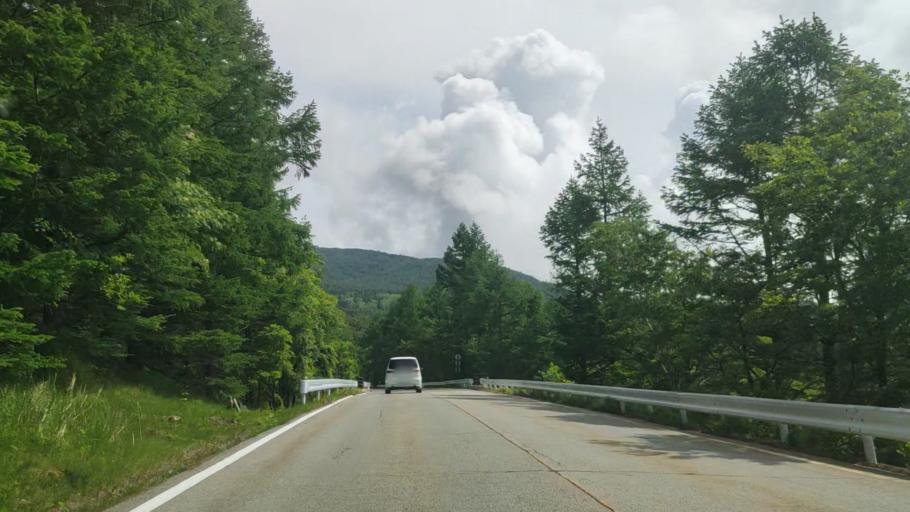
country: JP
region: Yamanashi
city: Fujikawaguchiko
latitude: 35.4131
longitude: 138.6997
